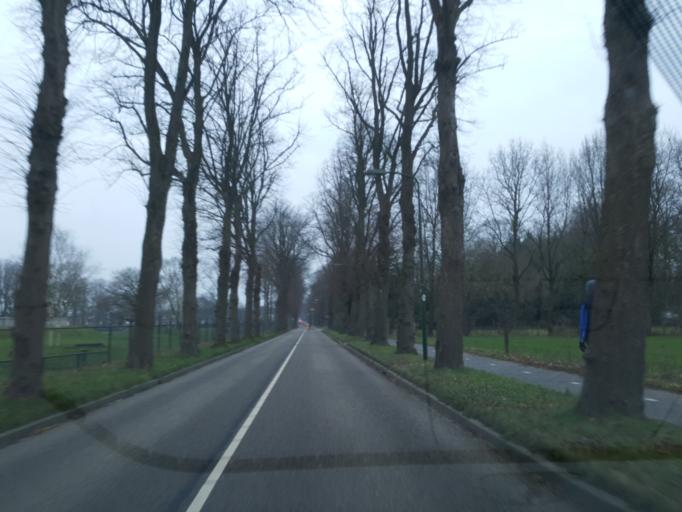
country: NL
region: North Holland
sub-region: Gemeente Wijdemeren
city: Nieuw-Loosdrecht
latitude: 52.2029
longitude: 5.1441
